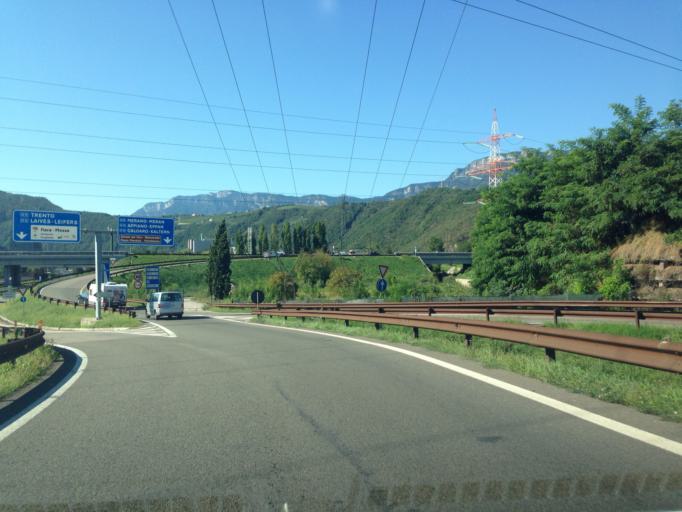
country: IT
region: Trentino-Alto Adige
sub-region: Bolzano
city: Bolzano
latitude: 46.4771
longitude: 11.3178
